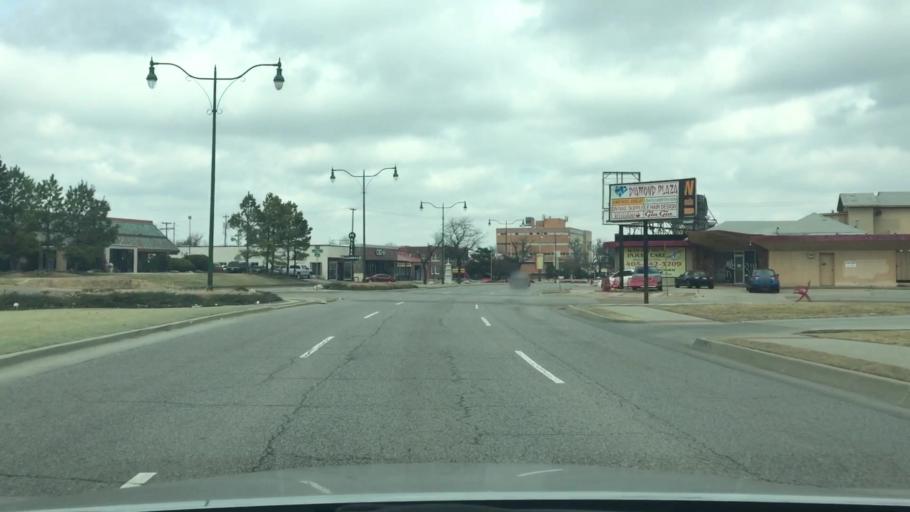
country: US
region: Oklahoma
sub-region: Oklahoma County
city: Oklahoma City
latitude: 35.4960
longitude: -97.5339
